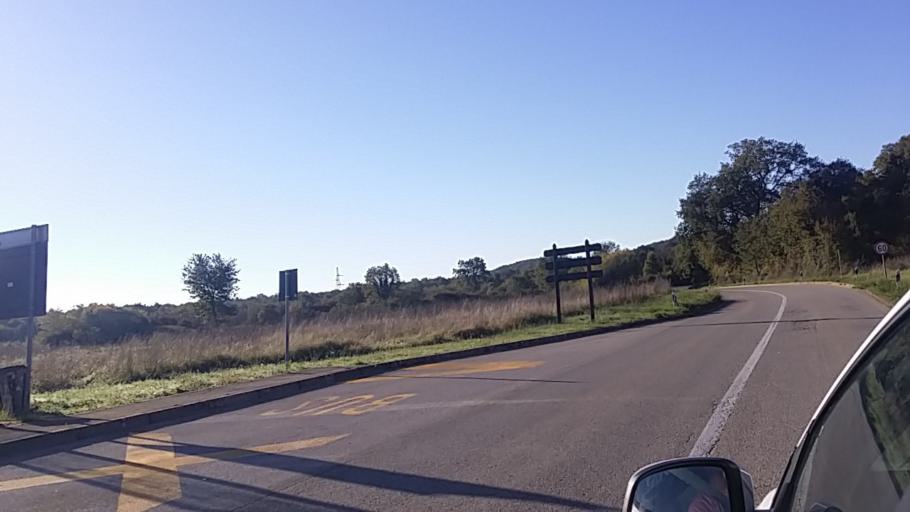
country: HR
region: Istarska
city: Vrsar
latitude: 45.1627
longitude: 13.6627
